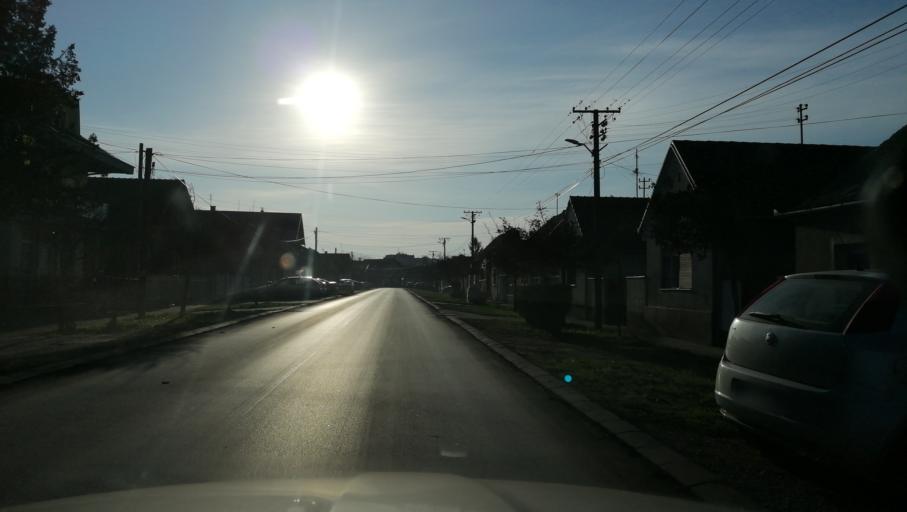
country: RS
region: Autonomna Pokrajina Vojvodina
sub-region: Sremski Okrug
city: Sremska Mitrovica
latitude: 44.9685
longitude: 19.6163
